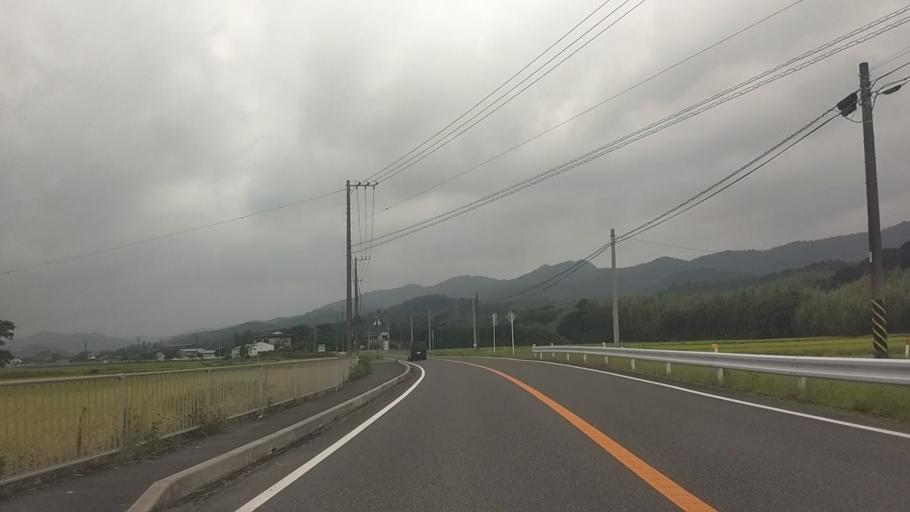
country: JP
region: Chiba
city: Kawaguchi
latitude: 35.1358
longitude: 139.9984
